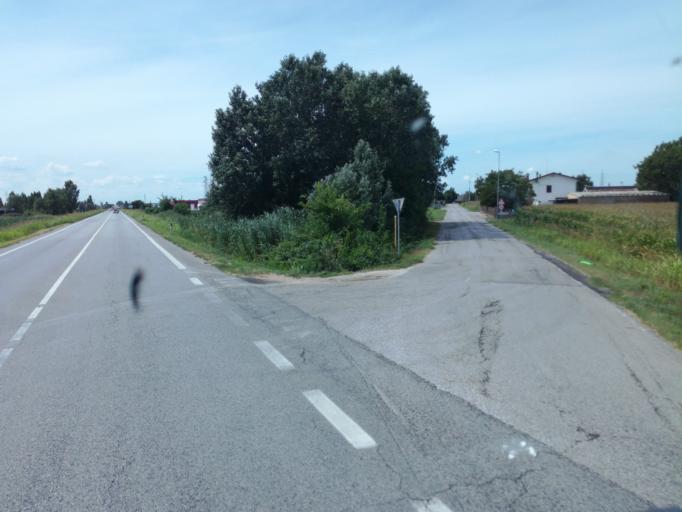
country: IT
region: Veneto
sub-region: Provincia di Rovigo
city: Rosolina
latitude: 45.0473
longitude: 12.2453
